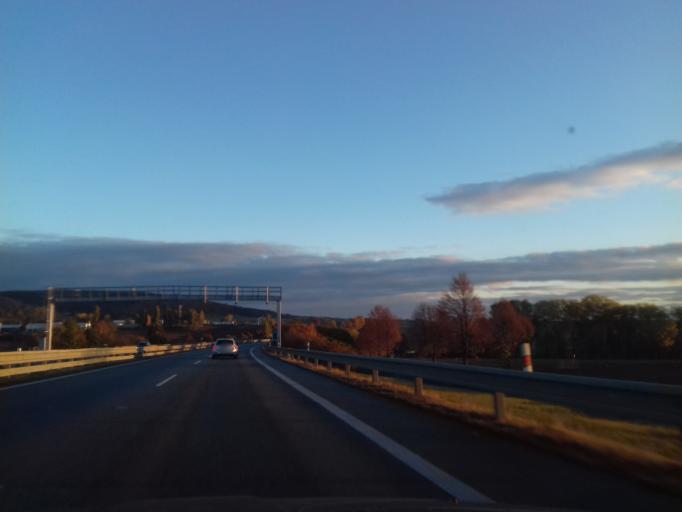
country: CZ
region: South Moravian
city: Pustimer
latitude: 49.3130
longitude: 17.0341
